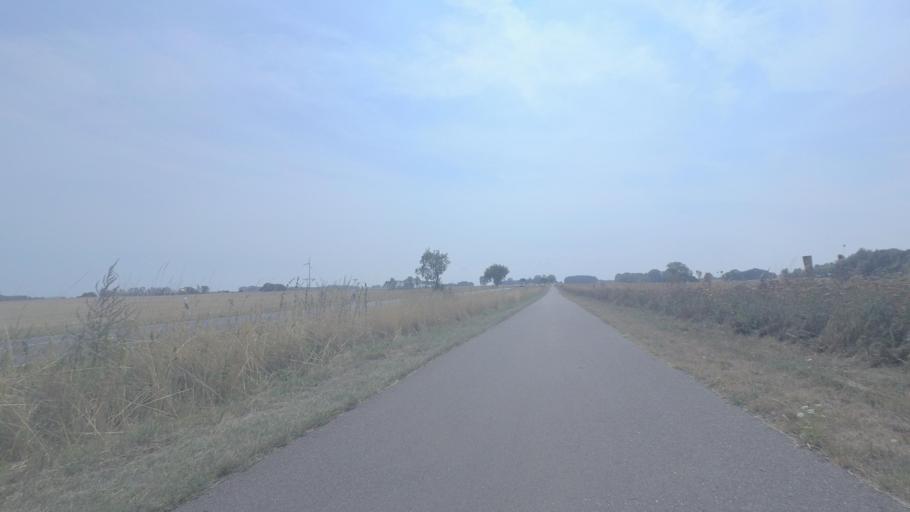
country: DE
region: Mecklenburg-Vorpommern
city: Garz
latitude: 54.3014
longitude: 13.3512
